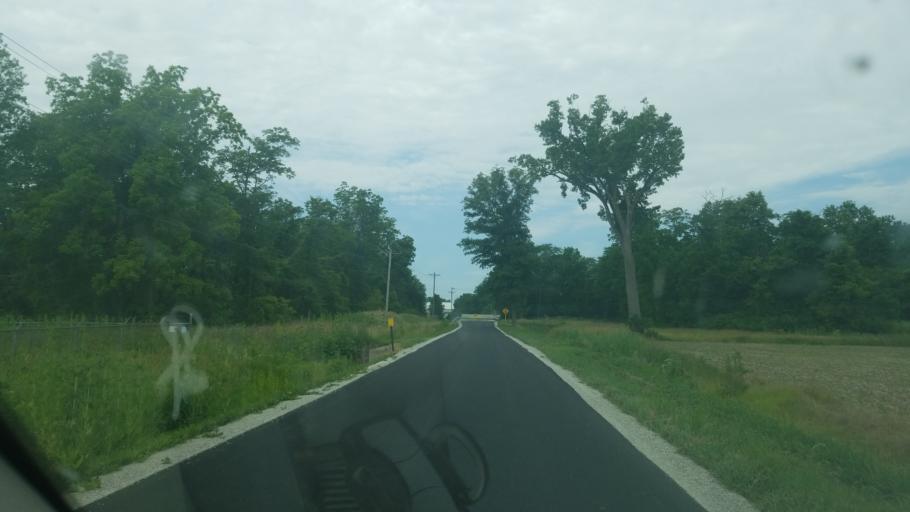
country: US
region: Ohio
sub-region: Wood County
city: North Baltimore
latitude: 41.2220
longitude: -83.6480
